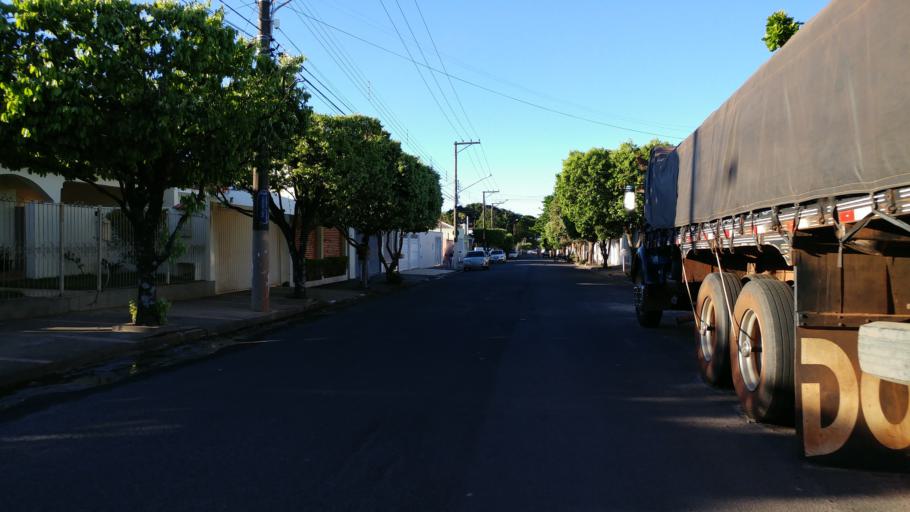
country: BR
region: Sao Paulo
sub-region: Paraguacu Paulista
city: Paraguacu Paulista
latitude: -22.4239
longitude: -50.5802
